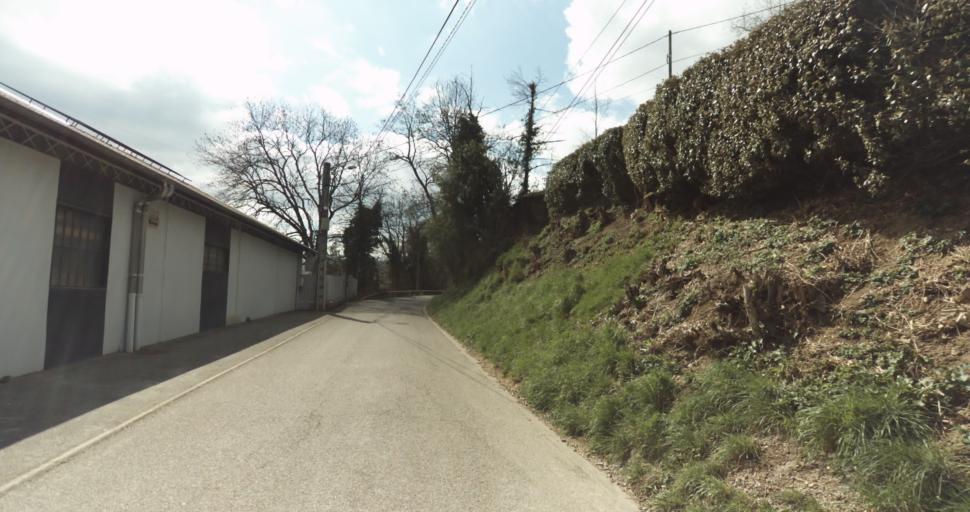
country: FR
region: Rhone-Alpes
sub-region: Departement du Rhone
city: Tarare
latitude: 45.9017
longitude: 4.4304
